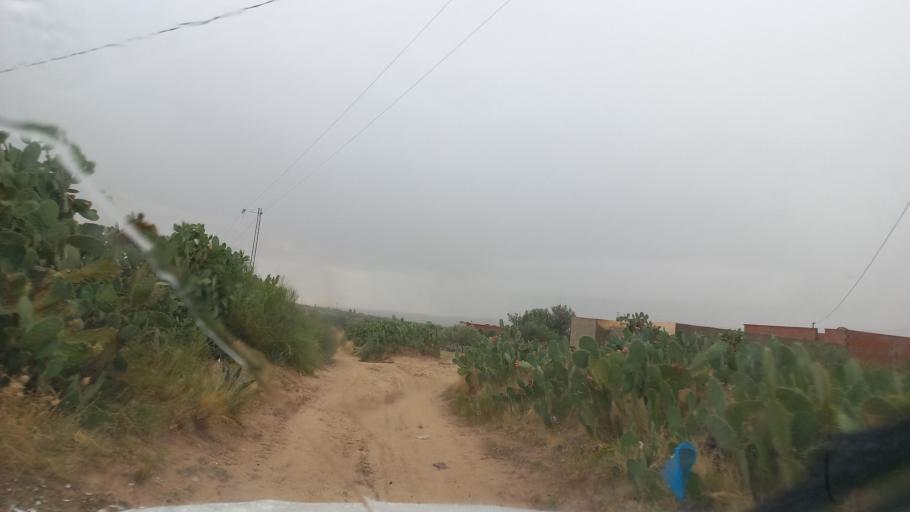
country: TN
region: Al Qasrayn
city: Kasserine
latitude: 35.2739
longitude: 8.9410
